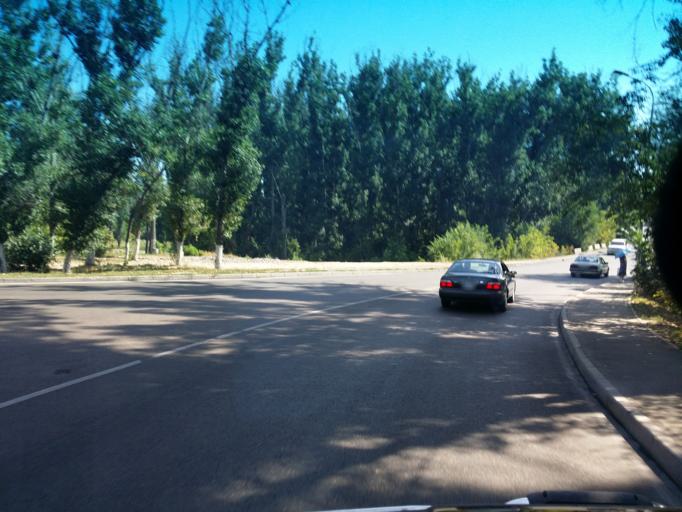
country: KZ
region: Almaty Oblysy
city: Pervomayskiy
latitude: 43.3364
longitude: 76.9353
